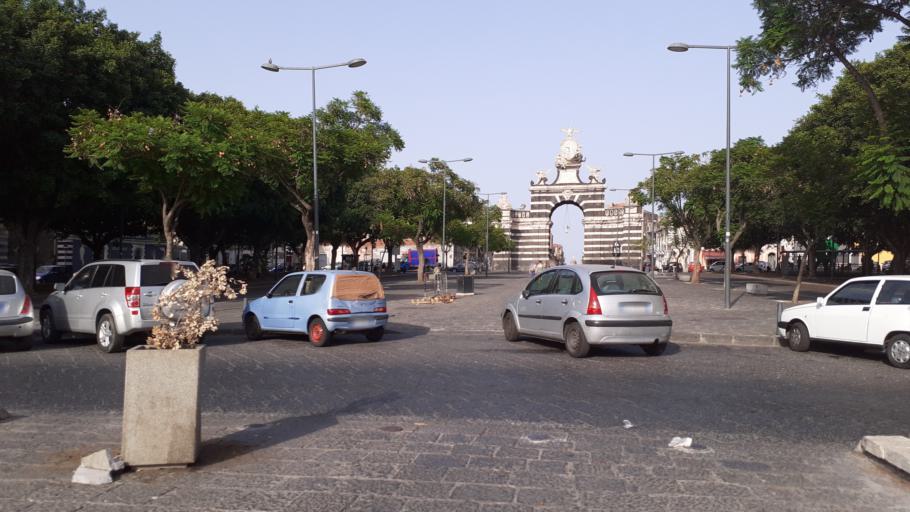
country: IT
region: Sicily
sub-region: Catania
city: Catania
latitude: 37.4993
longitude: 15.0723
